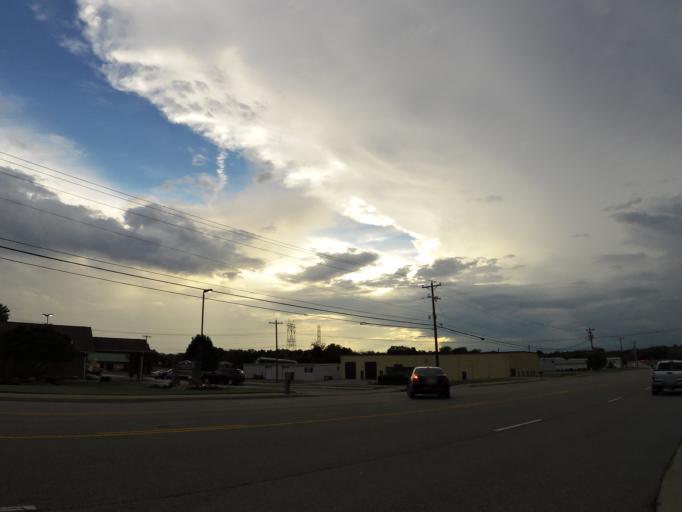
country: US
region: Tennessee
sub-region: Blount County
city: Maryville
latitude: 35.7682
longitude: -83.9960
